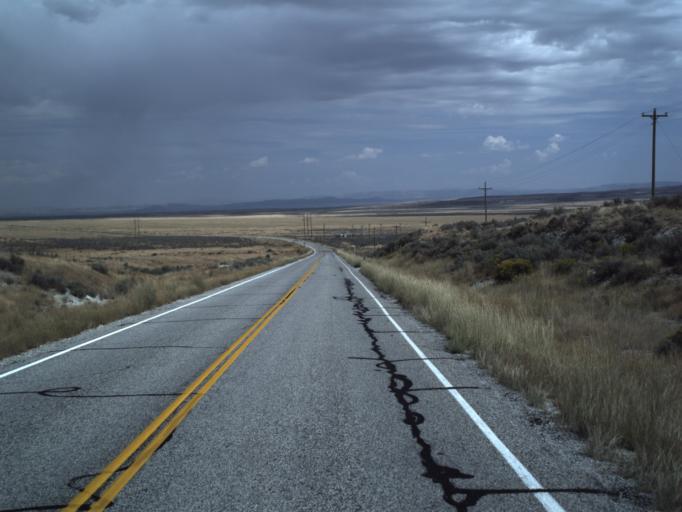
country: US
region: Idaho
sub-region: Minidoka County
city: Rupert
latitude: 41.8350
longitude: -113.1508
